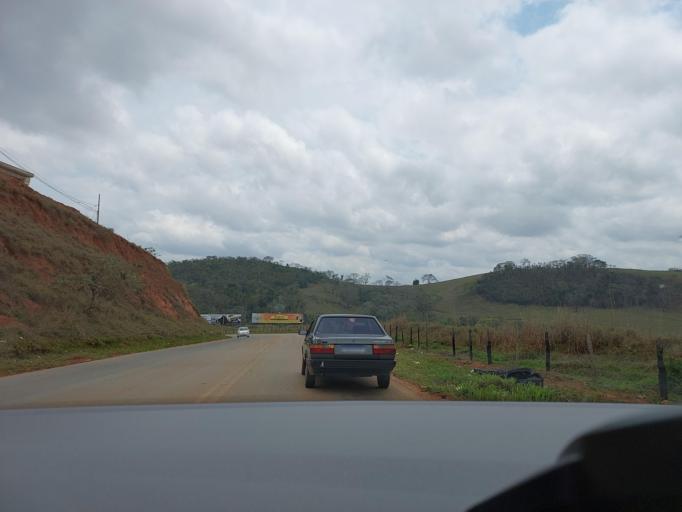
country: BR
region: Minas Gerais
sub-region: Ponte Nova
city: Ponte Nova
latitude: -20.3953
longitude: -42.8743
